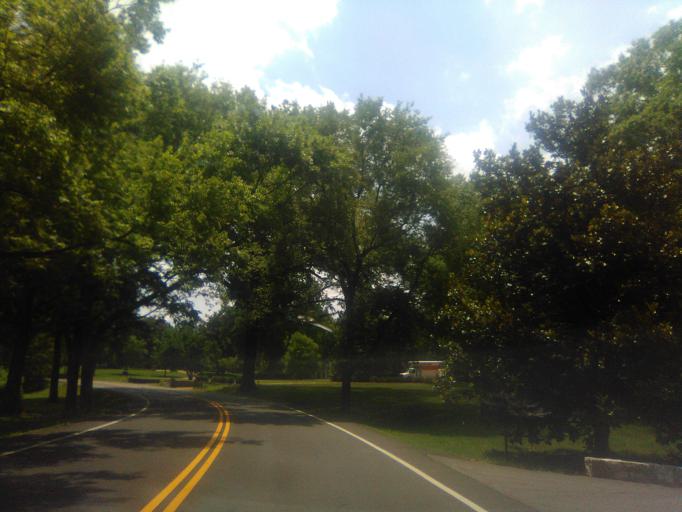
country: US
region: Tennessee
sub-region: Davidson County
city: Belle Meade
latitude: 36.0932
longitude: -86.8650
